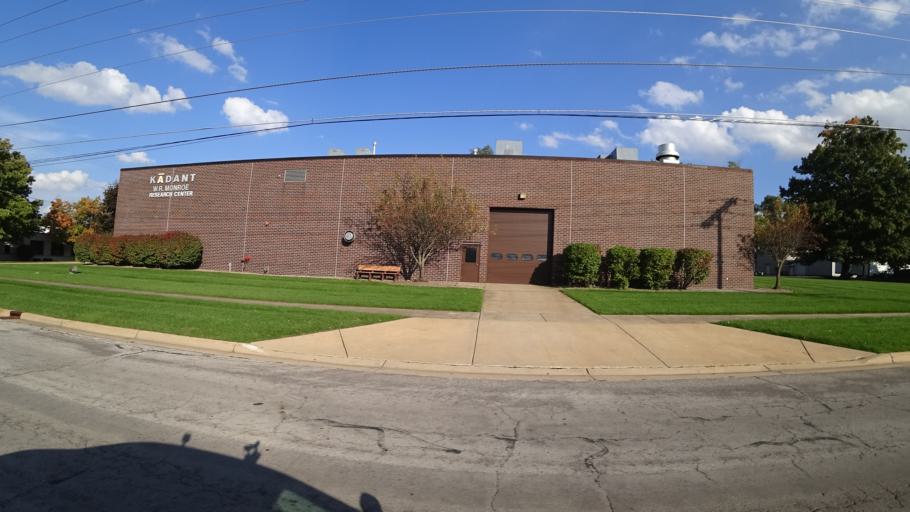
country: US
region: Michigan
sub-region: Saint Joseph County
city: Three Rivers
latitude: 41.9489
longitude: -85.6249
